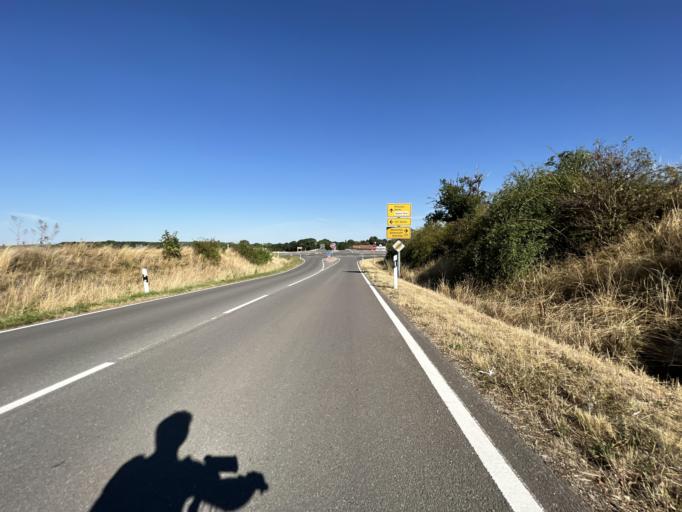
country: DE
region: North Rhine-Westphalia
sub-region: Regierungsbezirk Koln
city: Kreuzau
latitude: 50.7491
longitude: 6.4270
